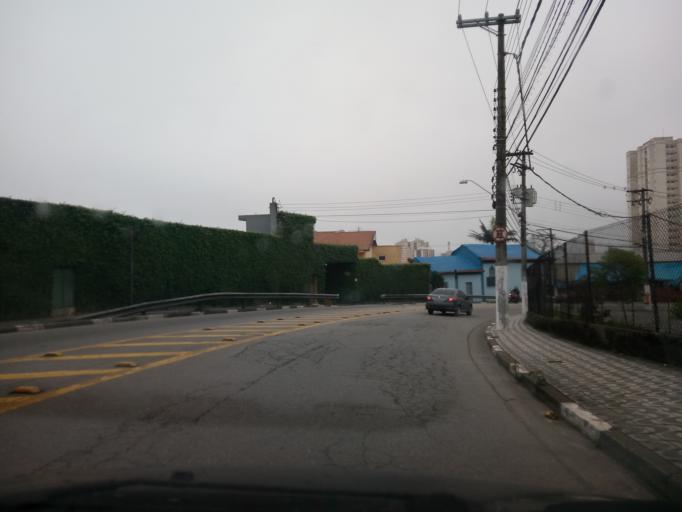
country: BR
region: Sao Paulo
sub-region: Sao Bernardo Do Campo
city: Sao Bernardo do Campo
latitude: -23.7319
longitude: -46.5692
